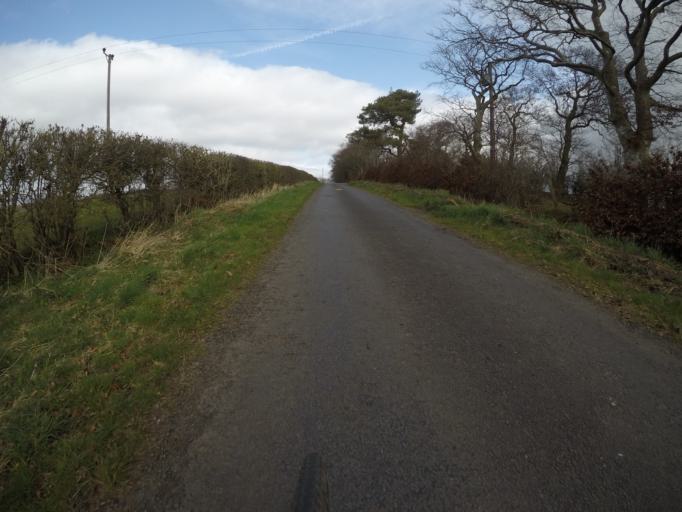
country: GB
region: Scotland
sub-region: North Ayrshire
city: Springside
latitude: 55.6572
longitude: -4.6101
